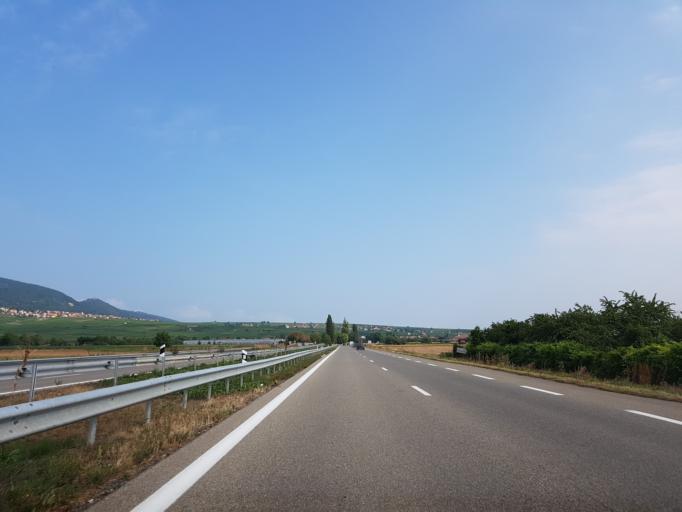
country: FR
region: Alsace
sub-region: Departement du Haut-Rhin
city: Pfaffenheim
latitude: 47.9973
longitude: 7.2943
